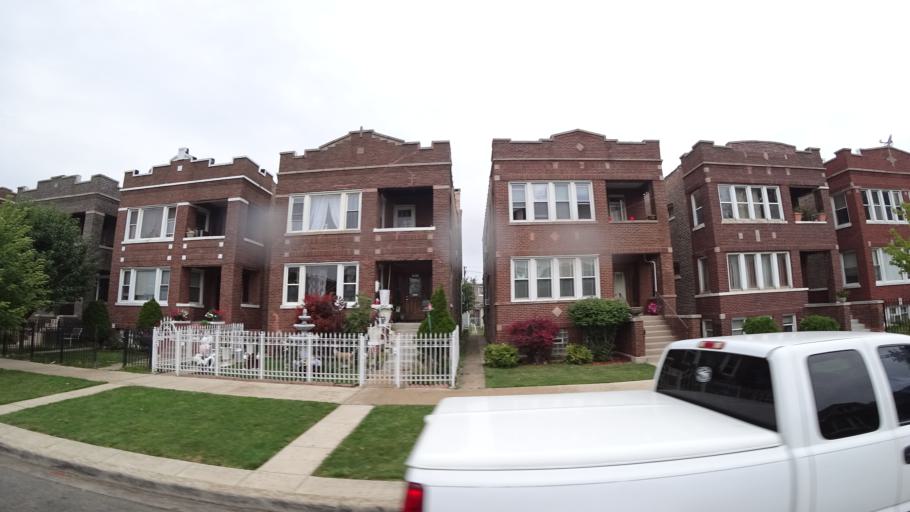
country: US
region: Illinois
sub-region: Cook County
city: Cicero
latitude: 41.8541
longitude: -87.7517
